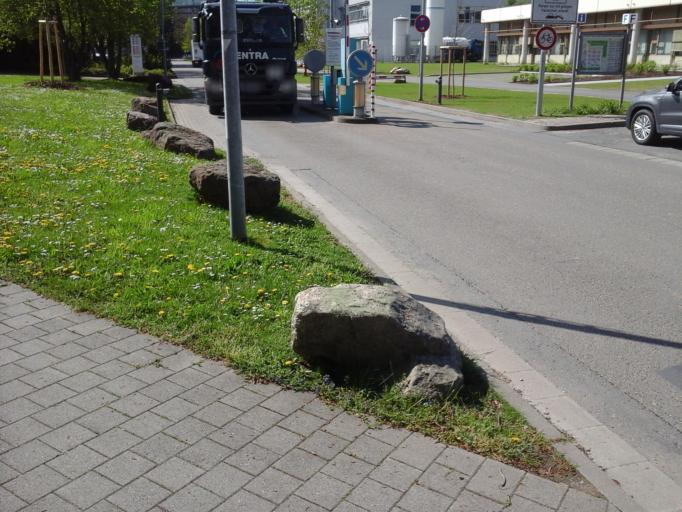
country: DE
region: Baden-Wuerttemberg
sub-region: Karlsruhe Region
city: Heidelberg
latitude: 49.4178
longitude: 8.6679
